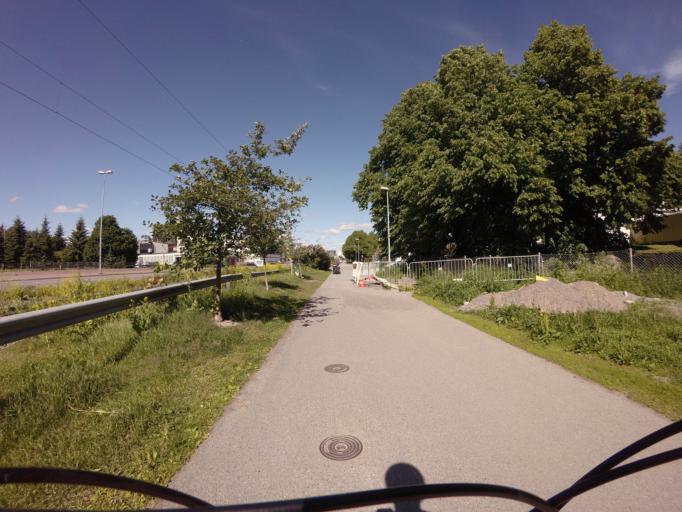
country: FI
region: Varsinais-Suomi
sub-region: Turku
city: Turku
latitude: 60.4452
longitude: 22.2364
